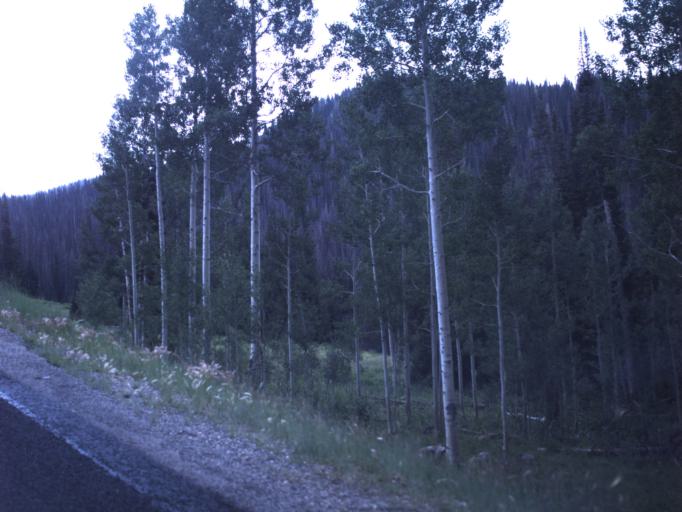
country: US
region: Utah
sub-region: Summit County
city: Francis
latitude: 40.4954
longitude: -111.0384
